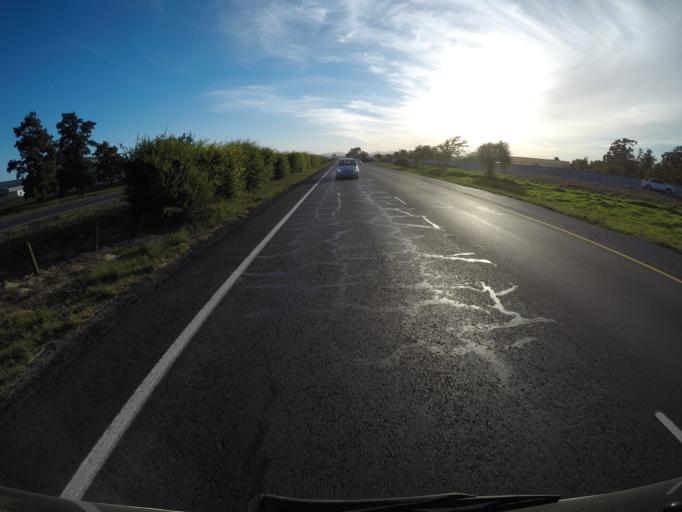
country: ZA
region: Western Cape
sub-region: City of Cape Town
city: Kraaifontein
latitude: -33.8358
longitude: 18.7341
